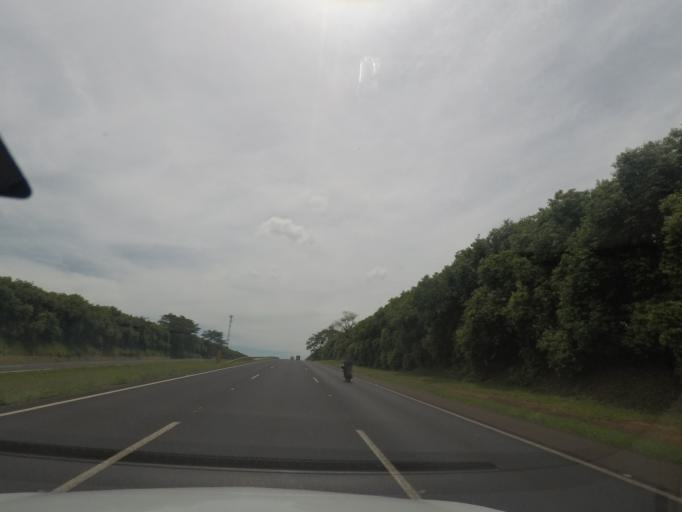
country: BR
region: Sao Paulo
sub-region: Bebedouro
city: Bebedouro
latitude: -20.9936
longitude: -48.4327
